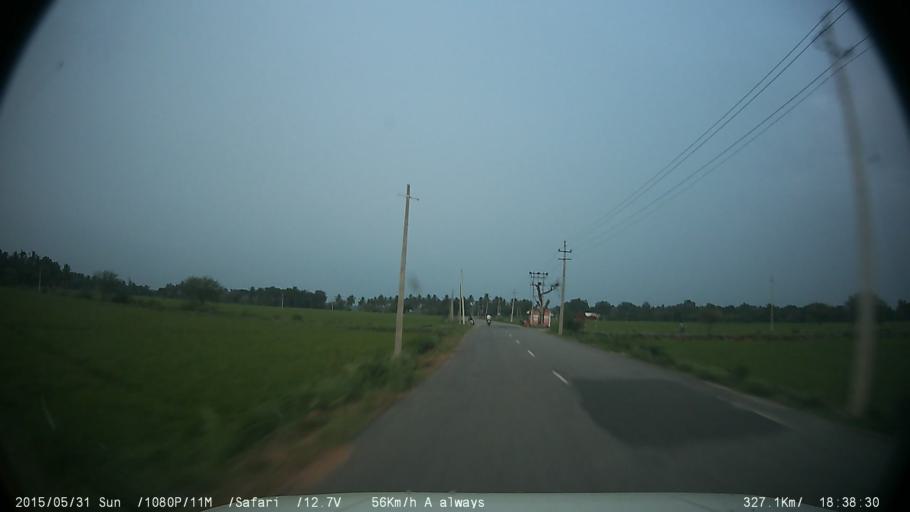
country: IN
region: Karnataka
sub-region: Mysore
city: Nanjangud
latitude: 12.1447
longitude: 76.7786
